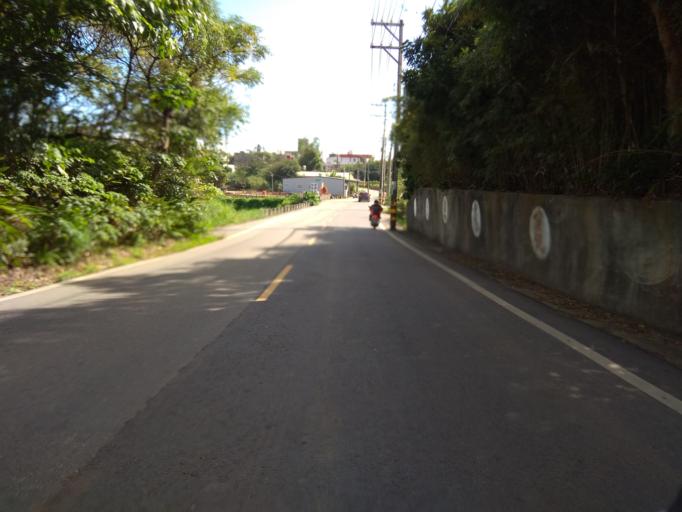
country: TW
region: Taiwan
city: Taoyuan City
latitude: 25.0400
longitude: 121.1265
